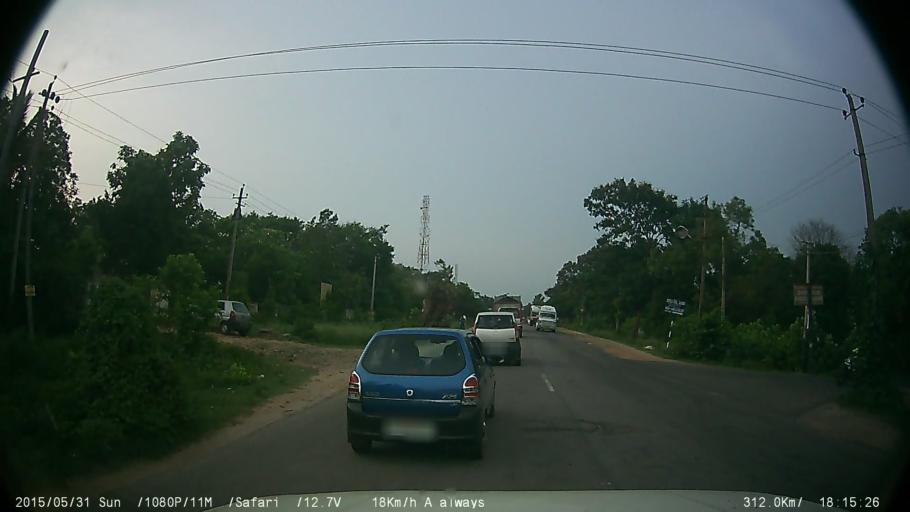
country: IN
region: Karnataka
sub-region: Mysore
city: Nanjangud
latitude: 12.1111
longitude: 76.6735
